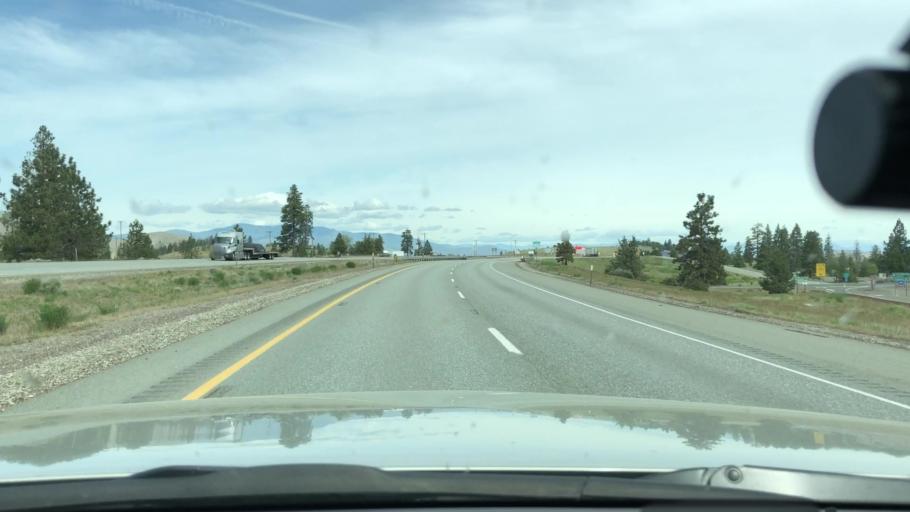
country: US
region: California
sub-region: Siskiyou County
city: Weed
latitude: 41.4405
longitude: -122.4338
